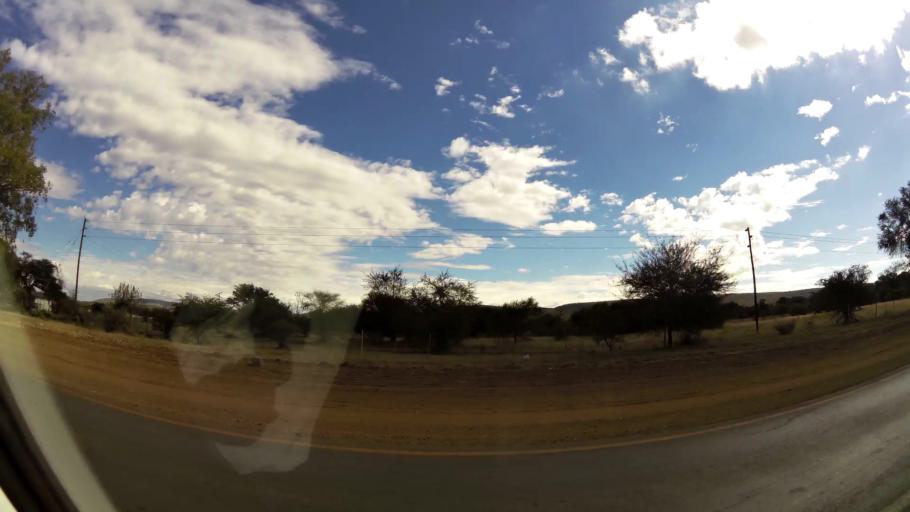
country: ZA
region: Limpopo
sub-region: Waterberg District Municipality
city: Bela-Bela
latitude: -24.8699
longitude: 28.3217
